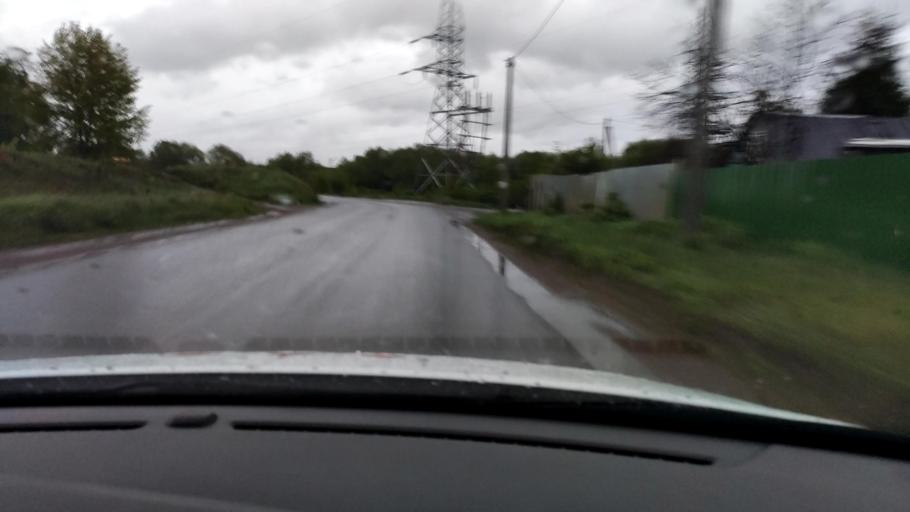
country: RU
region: Tatarstan
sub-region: Gorod Kazan'
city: Kazan
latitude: 55.7219
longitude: 49.1173
